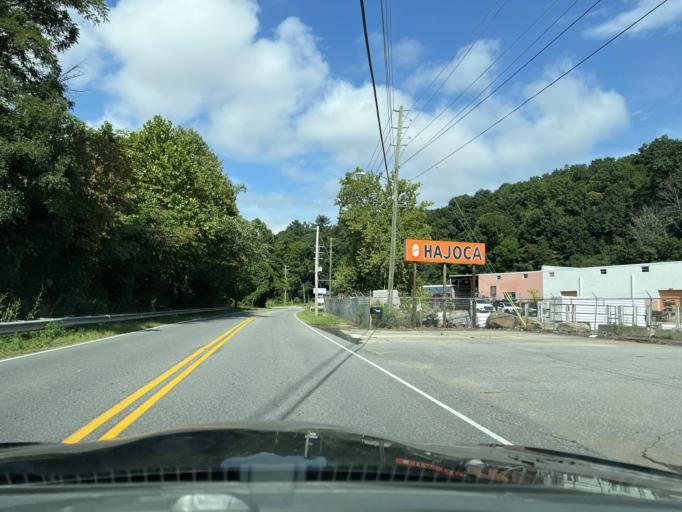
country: US
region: North Carolina
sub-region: Buncombe County
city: Asheville
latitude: 35.5722
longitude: -82.5321
